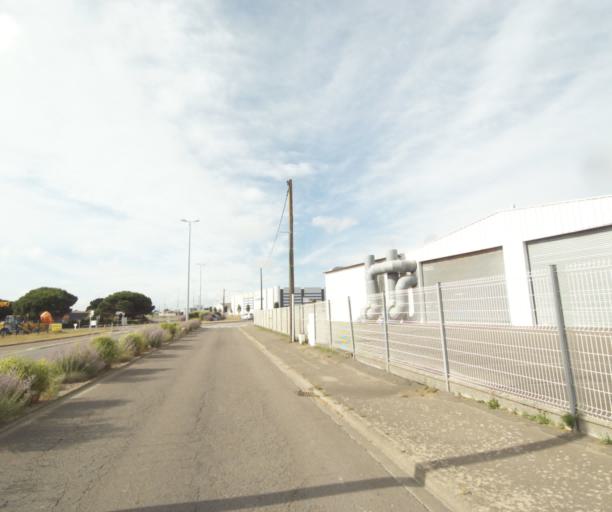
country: FR
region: Pays de la Loire
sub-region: Departement de la Vendee
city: Chateau-d'Olonne
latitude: 46.4888
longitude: -1.7322
